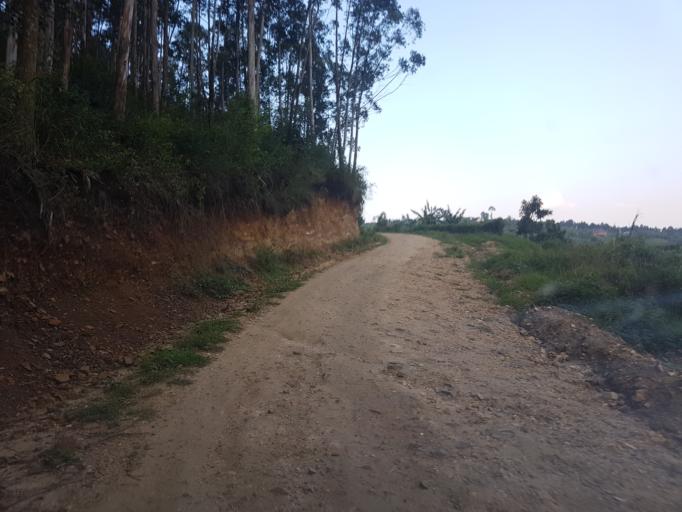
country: UG
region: Western Region
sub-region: Mitoma District
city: Mitoma
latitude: -0.6808
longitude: 29.9135
